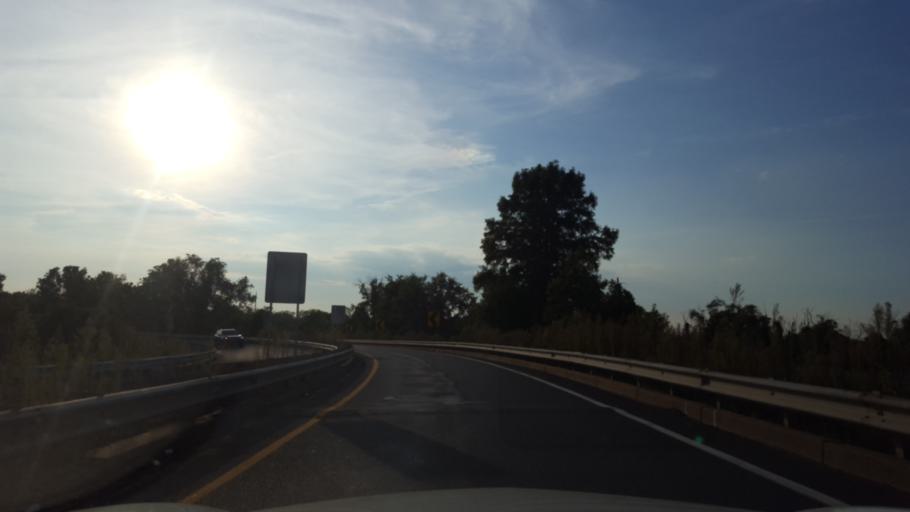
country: US
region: Delaware
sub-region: New Castle County
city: Newport
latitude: 39.7061
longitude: -75.6028
